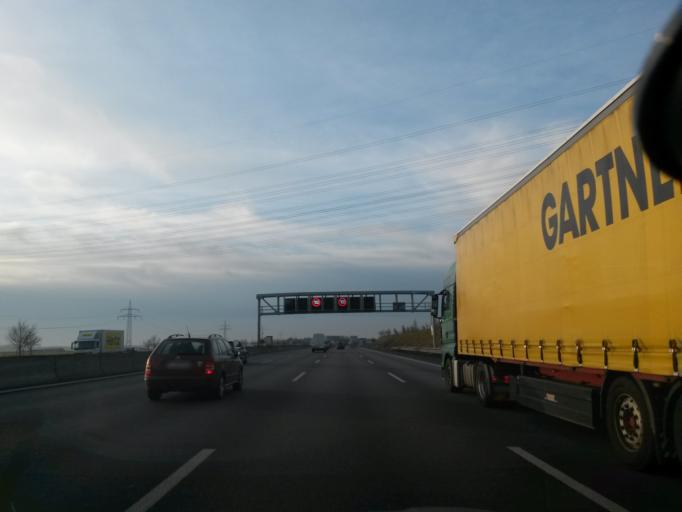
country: DE
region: Bavaria
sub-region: Upper Bavaria
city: Eching
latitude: 48.2869
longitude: 11.6378
